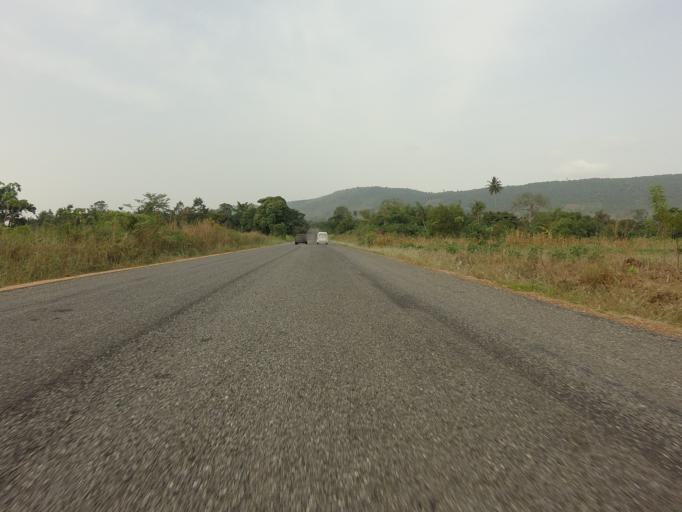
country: GH
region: Volta
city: Ho
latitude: 6.4405
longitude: 0.2038
